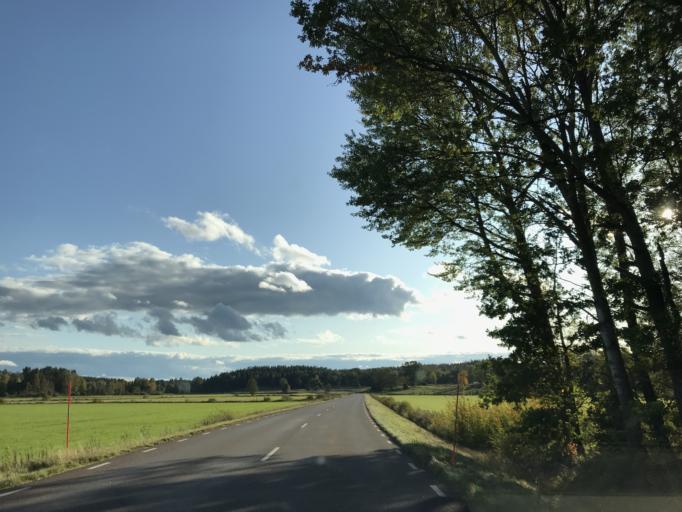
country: SE
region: Kalmar
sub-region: Hultsfreds Kommun
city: Virserum
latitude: 57.3531
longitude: 15.6103
